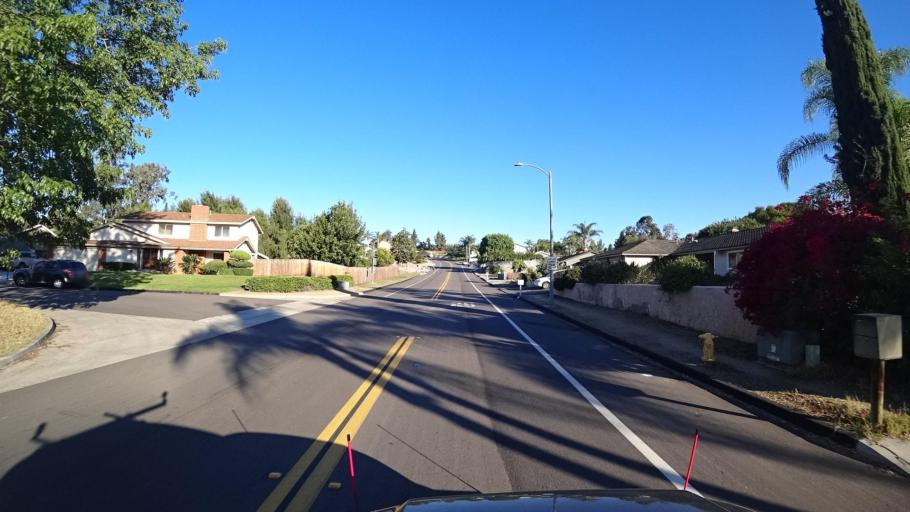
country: US
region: California
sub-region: San Diego County
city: Bonita
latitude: 32.6700
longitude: -117.0303
